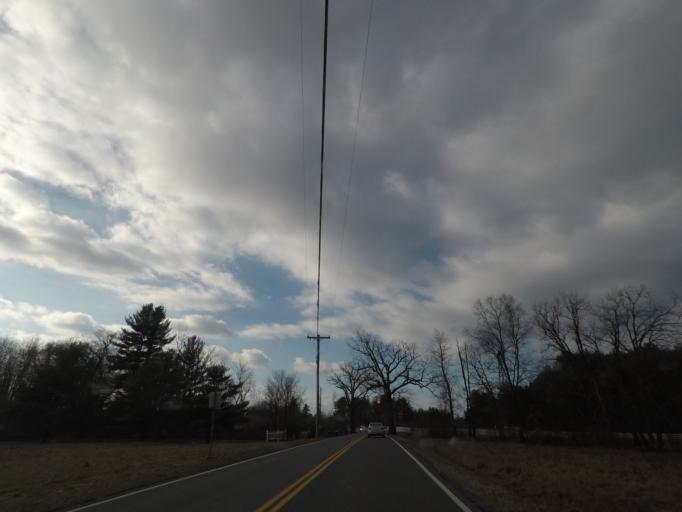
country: US
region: New York
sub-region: Albany County
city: McKownville
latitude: 42.6665
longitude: -73.8654
